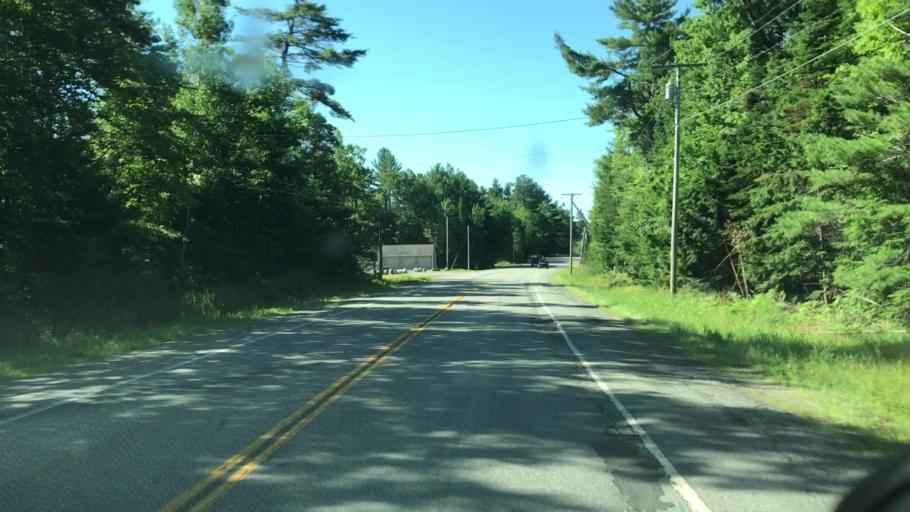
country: US
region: Maine
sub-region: Penobscot County
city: Howland
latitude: 45.2552
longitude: -68.6377
